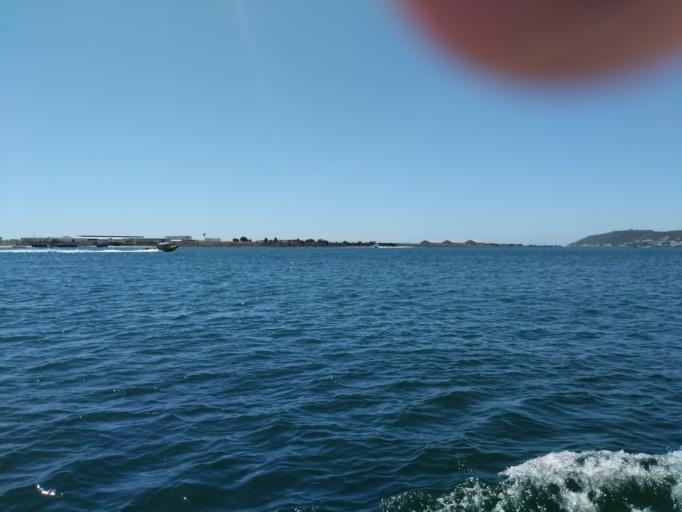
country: US
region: California
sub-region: San Diego County
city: Coronado
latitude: 32.7130
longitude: -117.2231
